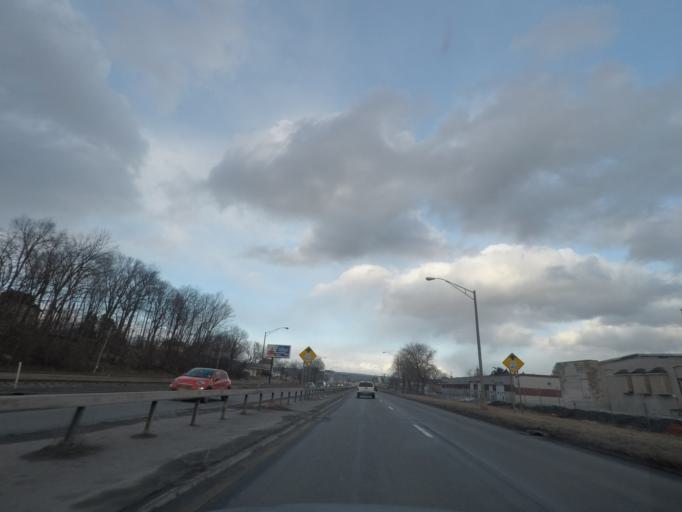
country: US
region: New York
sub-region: Oneida County
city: Yorkville
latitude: 43.0947
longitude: -75.2575
